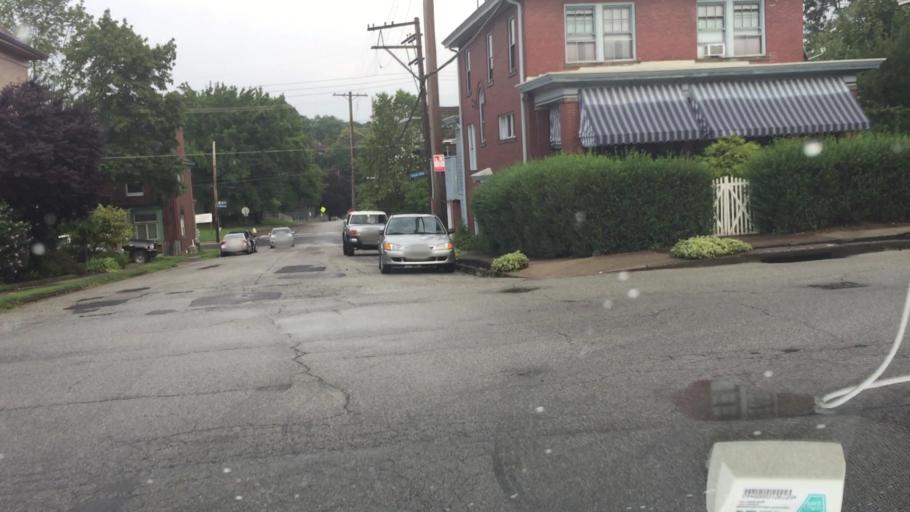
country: US
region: Pennsylvania
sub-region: Allegheny County
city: Sharpsburg
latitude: 40.4773
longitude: -79.9303
